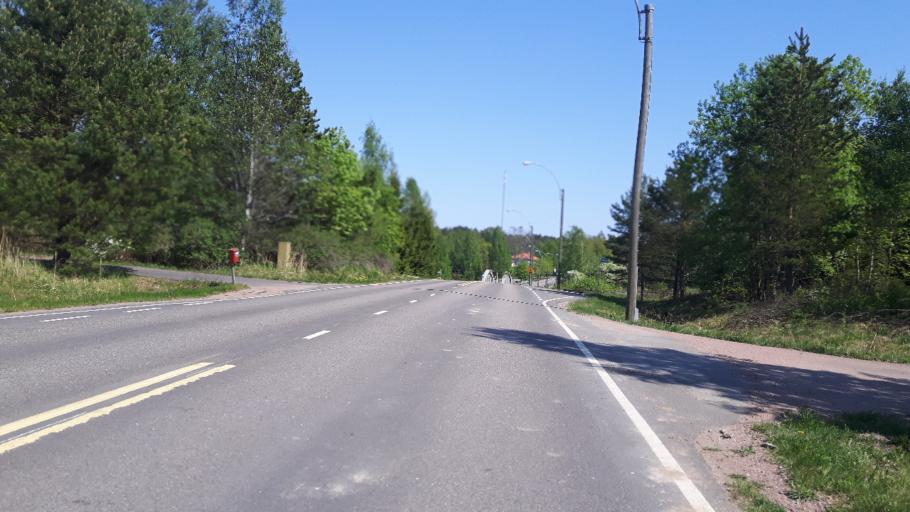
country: FI
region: Kymenlaakso
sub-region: Kotka-Hamina
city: Broby
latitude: 60.4954
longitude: 26.7130
